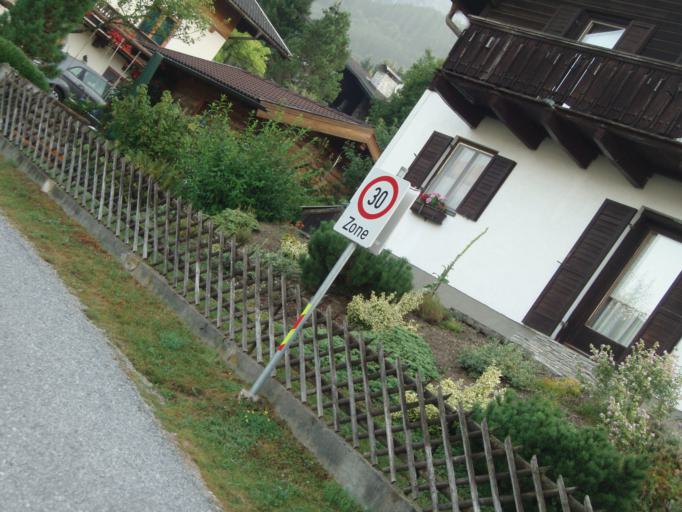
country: AT
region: Salzburg
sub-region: Politischer Bezirk Sankt Johann im Pongau
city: Pfarrwerfen
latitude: 47.4659
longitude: 13.2073
